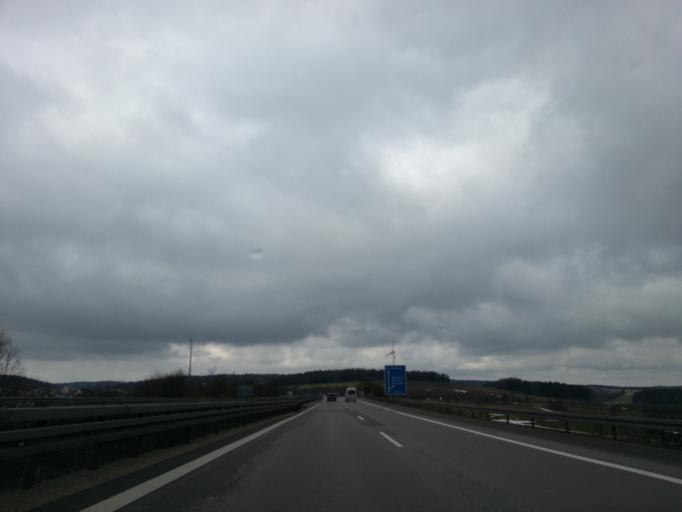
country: DE
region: Bavaria
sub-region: Upper Palatinate
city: Brunn
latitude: 49.1379
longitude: 11.8629
